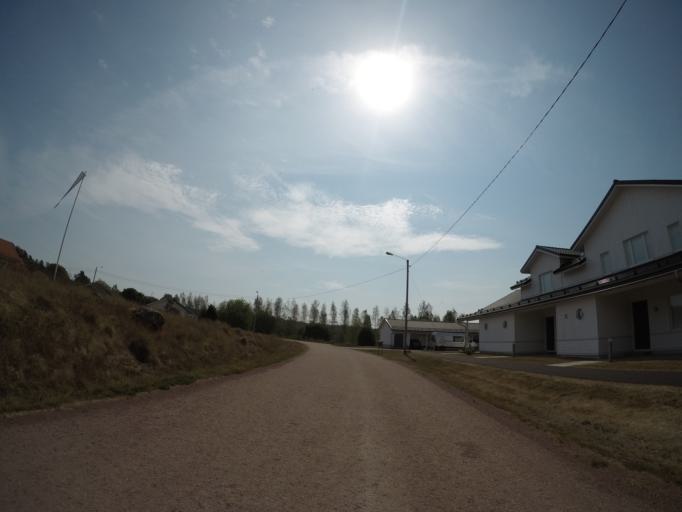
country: AX
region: Alands landsbygd
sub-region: Finstroem
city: Finstroem
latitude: 60.2314
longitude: 19.9964
